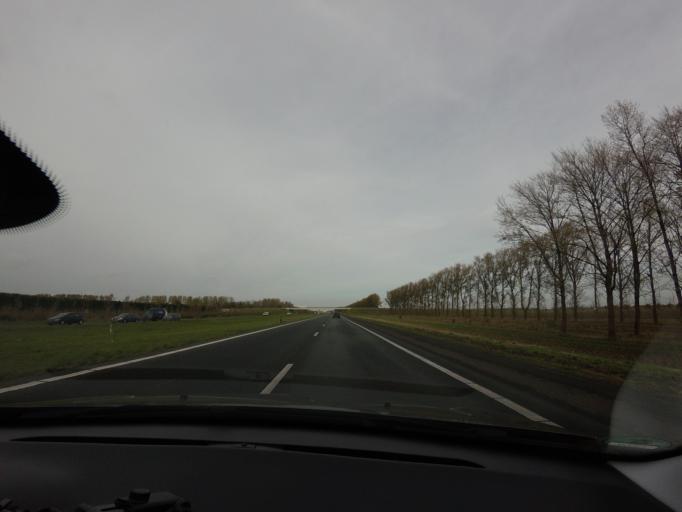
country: NL
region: Flevoland
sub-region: Gemeente Lelystad
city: Lelystad
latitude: 52.5168
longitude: 5.5337
